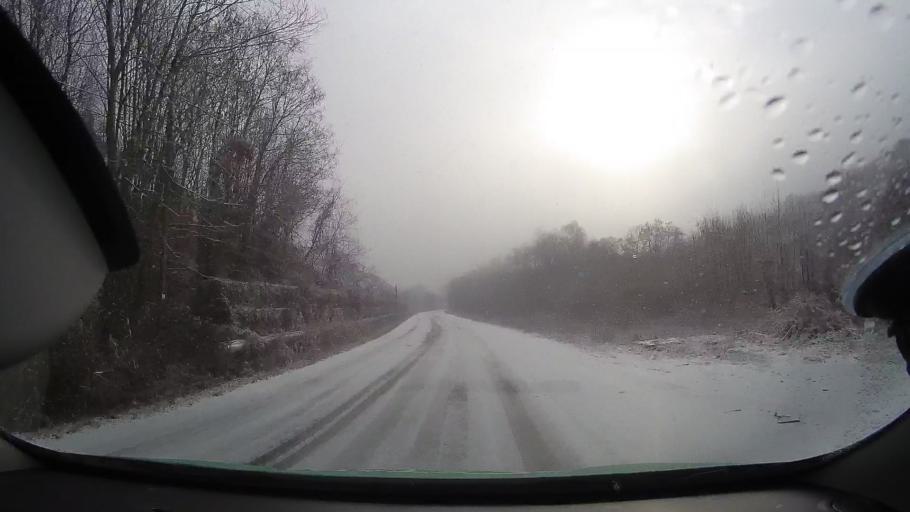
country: RO
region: Alba
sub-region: Comuna Livezile
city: Livezile
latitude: 46.3596
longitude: 23.6123
